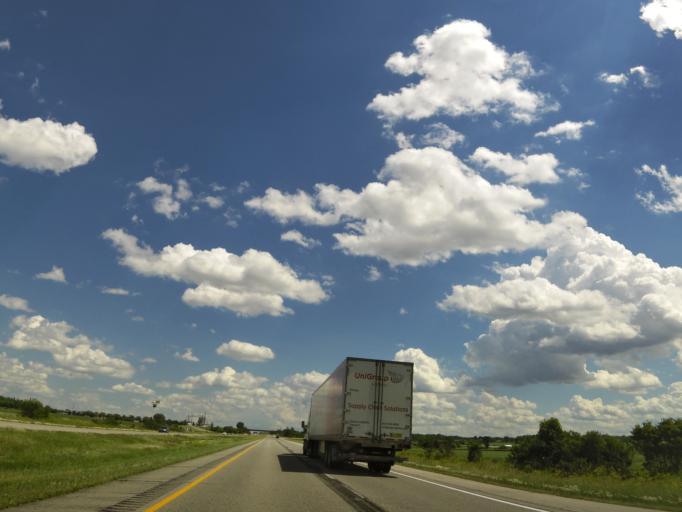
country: US
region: Iowa
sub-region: Linn County
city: Center Point
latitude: 42.1765
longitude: -91.7880
